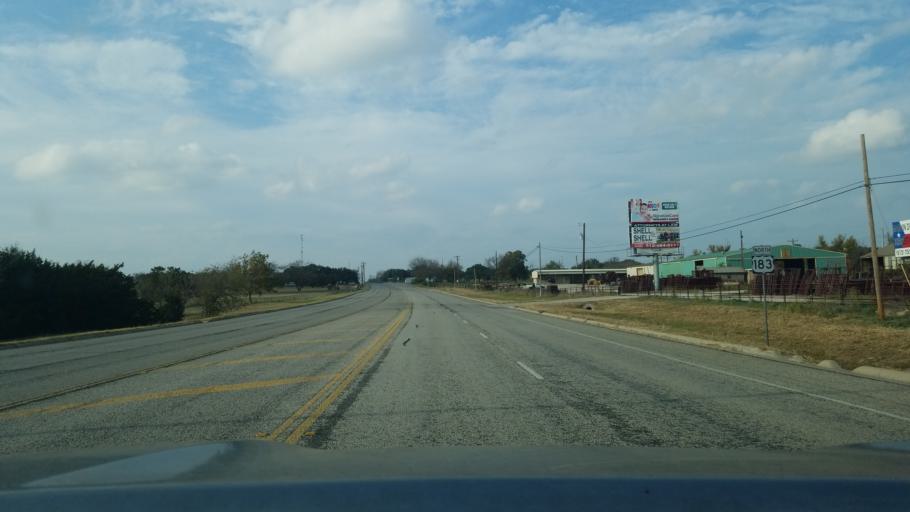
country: US
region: Texas
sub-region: Lampasas County
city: Lampasas
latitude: 31.2082
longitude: -98.3891
